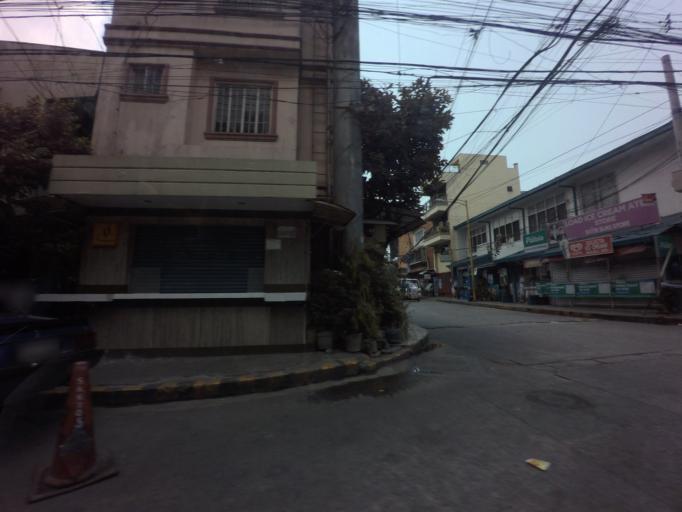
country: PH
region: Metro Manila
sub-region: Makati City
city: Makati City
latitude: 14.5645
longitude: 121.0399
